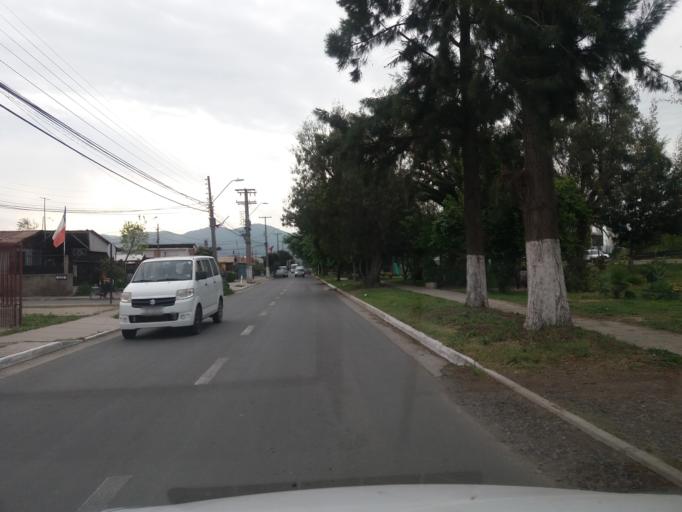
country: CL
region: Valparaiso
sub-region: Provincia de Quillota
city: Hacienda La Calera
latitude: -32.7845
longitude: -71.1733
